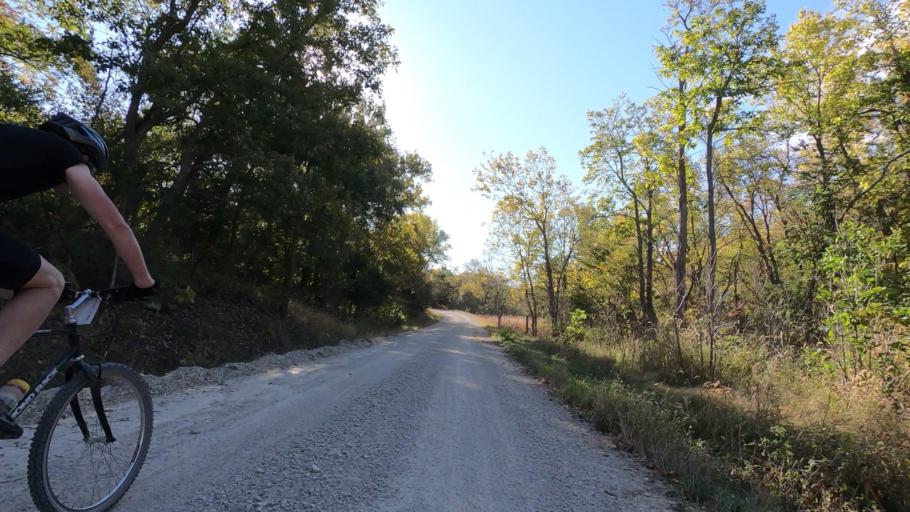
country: US
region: Kansas
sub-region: Pottawatomie County
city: Westmoreland
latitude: 39.4809
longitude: -96.5901
